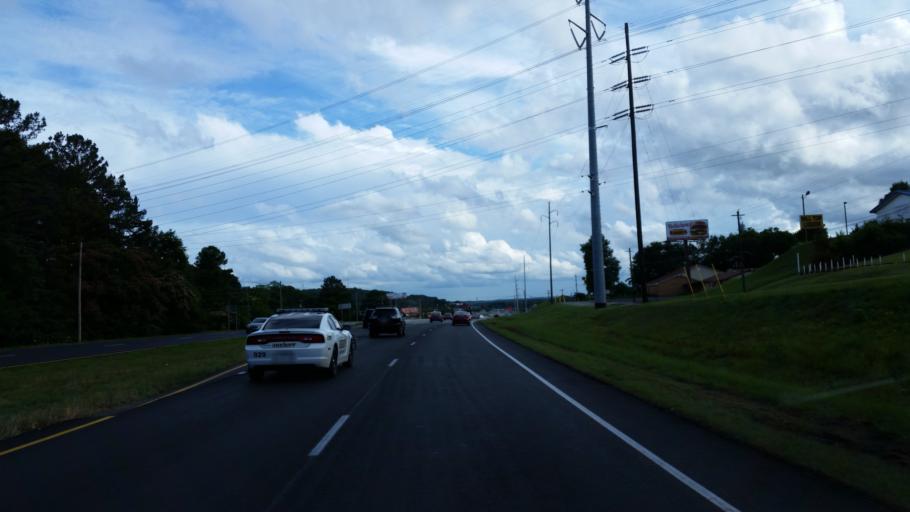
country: US
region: Georgia
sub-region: Bartow County
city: Cartersville
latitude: 34.1795
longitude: -84.7856
